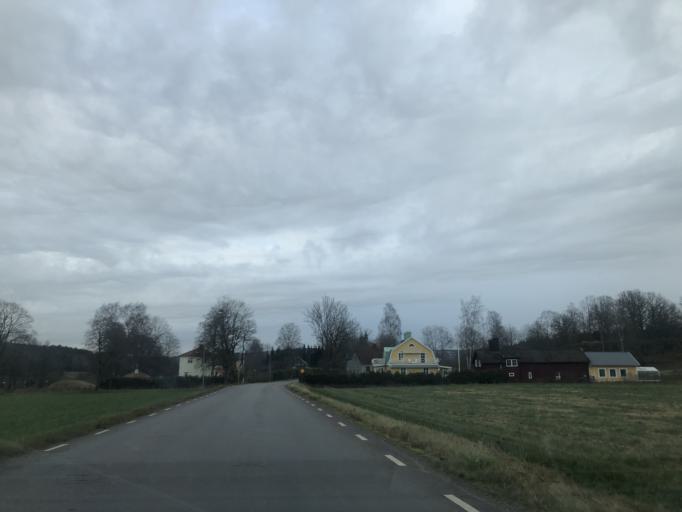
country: SE
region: Vaestra Goetaland
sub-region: Ulricehamns Kommun
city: Ulricehamn
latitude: 57.7983
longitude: 13.3716
